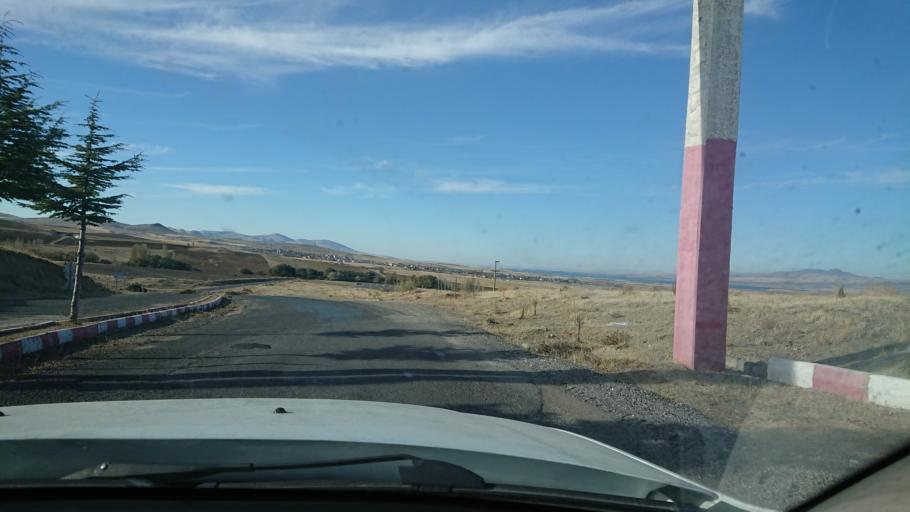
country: TR
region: Aksaray
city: Sariyahsi
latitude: 38.9678
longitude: 33.8720
